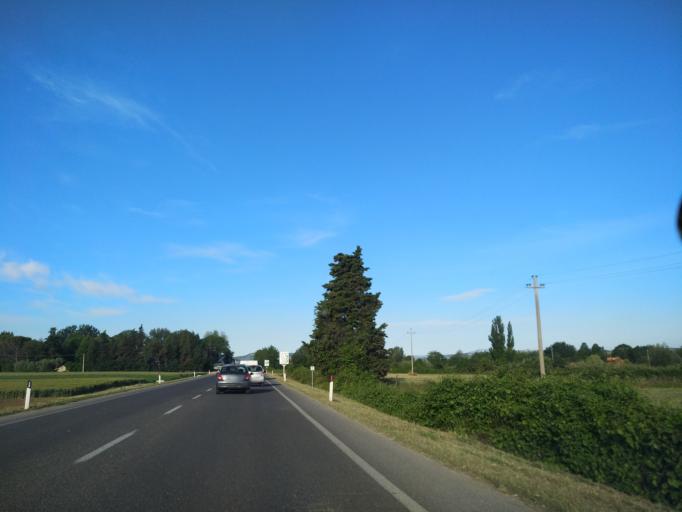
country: IT
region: The Marches
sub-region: Provincia di Pesaro e Urbino
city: Villa Ceccolini
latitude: 43.8726
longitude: 12.8383
